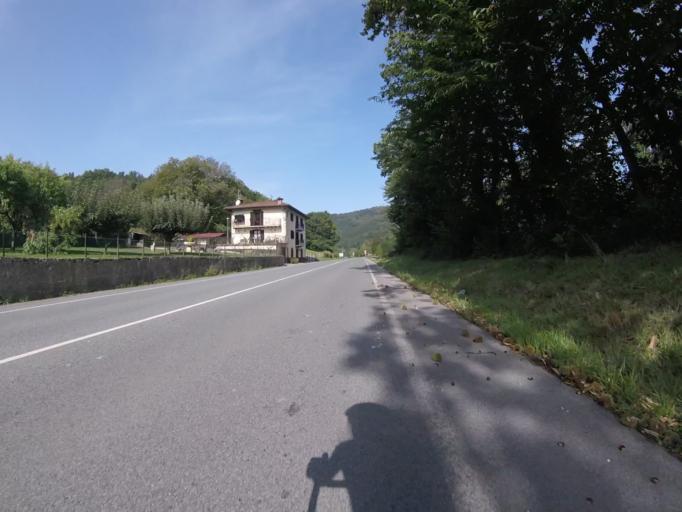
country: ES
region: Navarre
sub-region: Provincia de Navarra
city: Doneztebe
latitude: 43.1393
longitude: -1.5591
